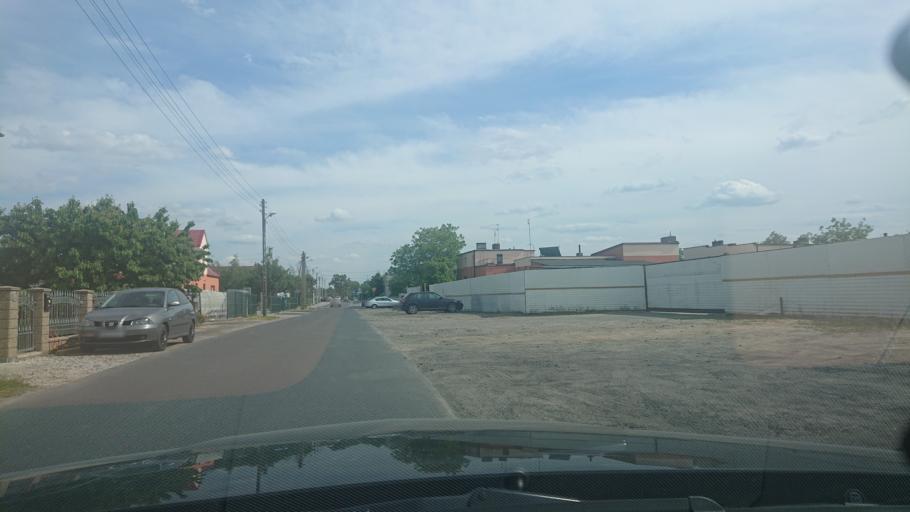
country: PL
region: Greater Poland Voivodeship
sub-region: Powiat gnieznienski
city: Gniezno
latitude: 52.5237
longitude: 17.6102
